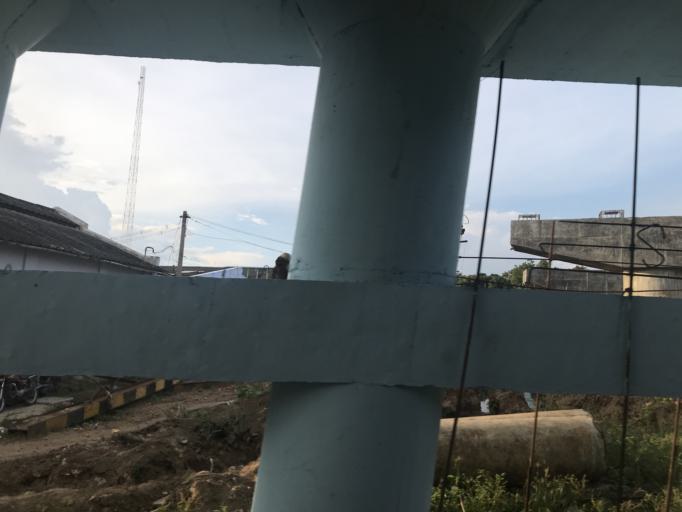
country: IN
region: Tamil Nadu
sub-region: Coimbatore
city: Coimbatore
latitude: 11.0292
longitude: 76.9805
